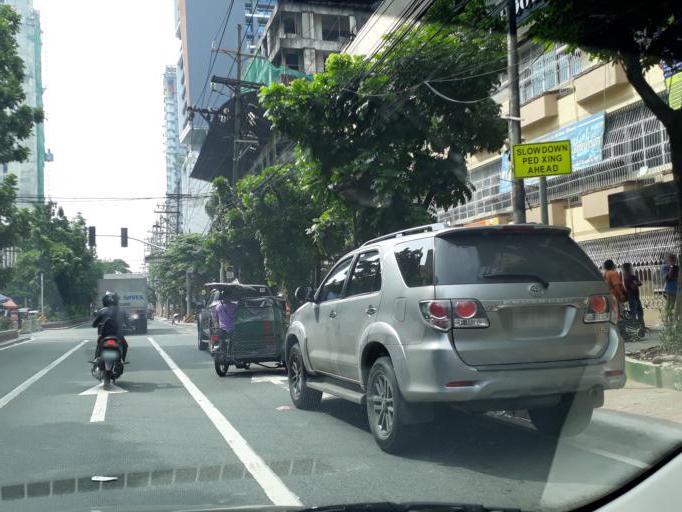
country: PH
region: Metro Manila
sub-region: City of Manila
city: Manila
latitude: 14.6114
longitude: 120.9910
